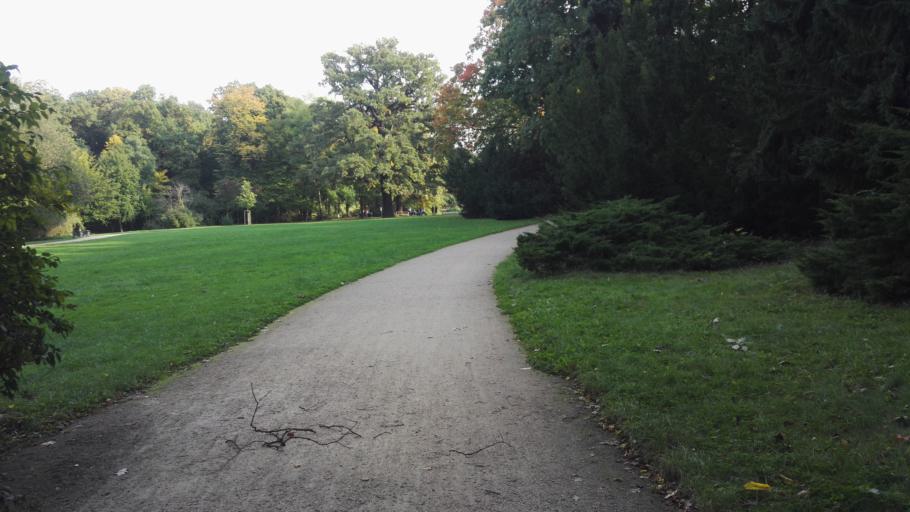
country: DE
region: Saxony
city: Dresden
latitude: 51.0345
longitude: 13.7627
